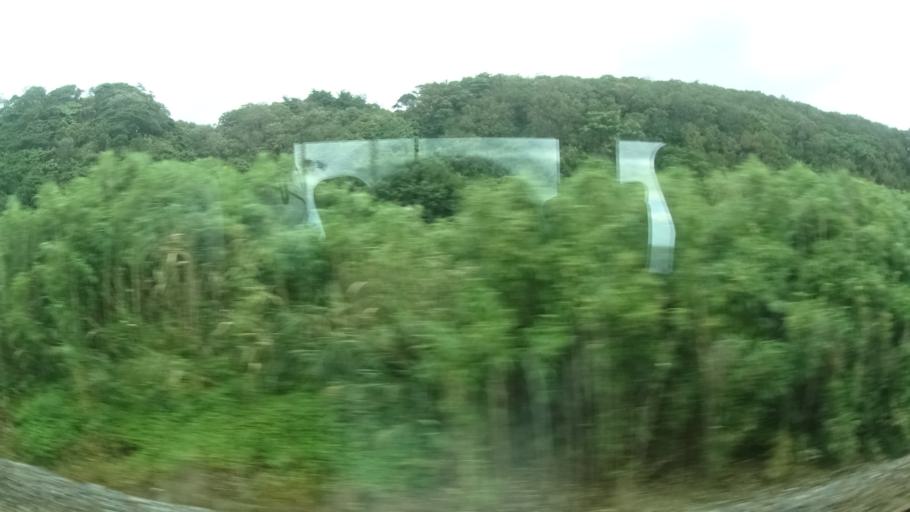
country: JP
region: Niigata
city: Murakami
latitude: 38.2628
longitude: 139.4475
